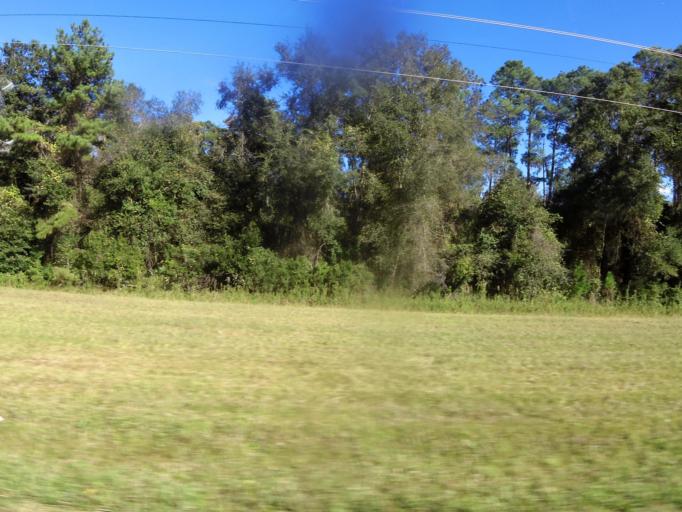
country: US
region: Florida
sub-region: Alachua County
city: Alachua
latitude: 29.7241
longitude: -82.3888
